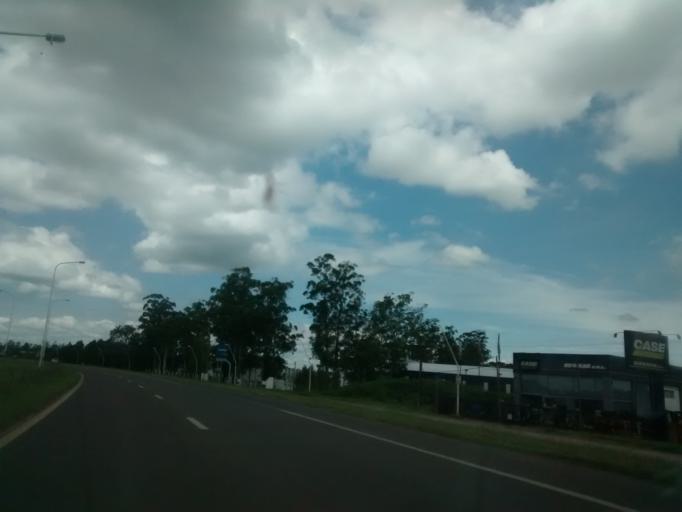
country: AR
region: Chaco
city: Fontana
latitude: -27.4127
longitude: -58.9983
